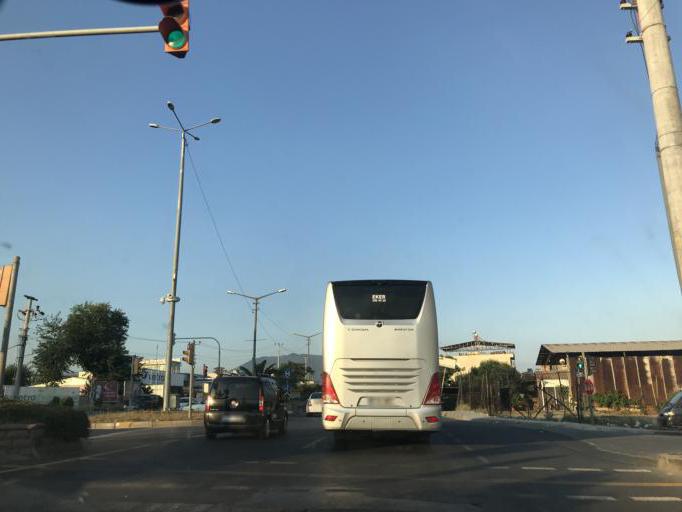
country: TR
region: Aydin
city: Nazilli
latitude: 37.9131
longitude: 28.3451
